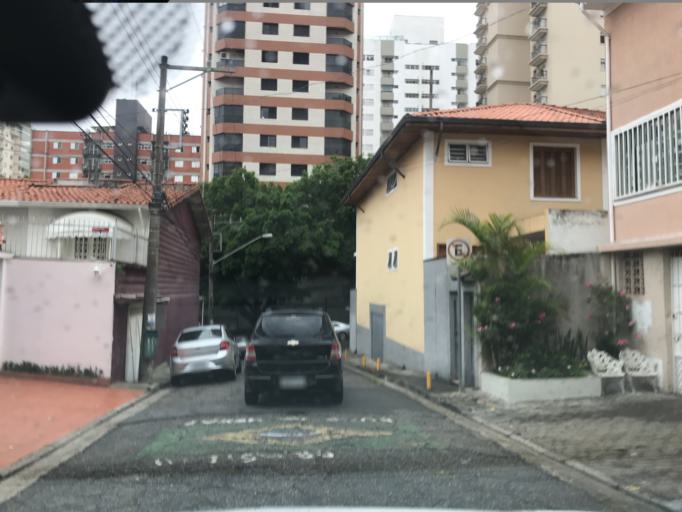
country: BR
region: Sao Paulo
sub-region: Sao Paulo
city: Sao Paulo
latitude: -23.5371
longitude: -46.6805
